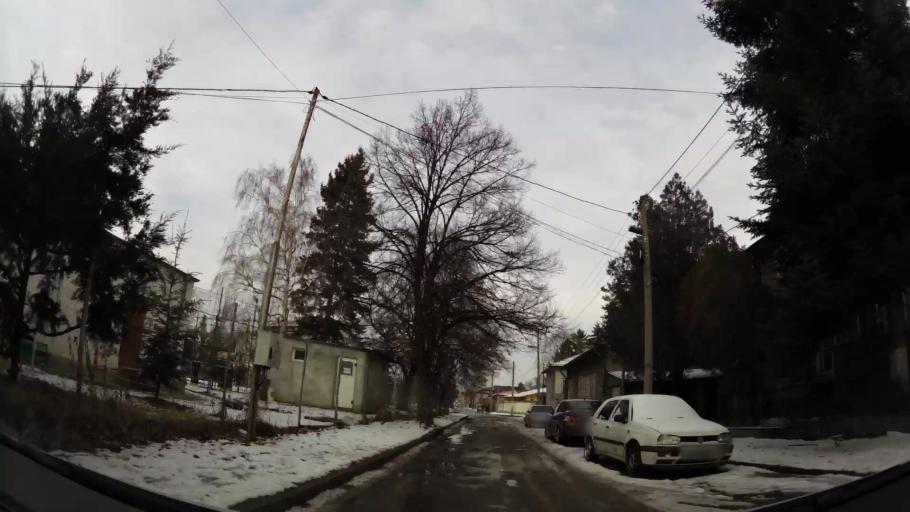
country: BG
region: Sofia-Capital
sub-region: Stolichna Obshtina
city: Sofia
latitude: 42.7147
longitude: 23.3457
